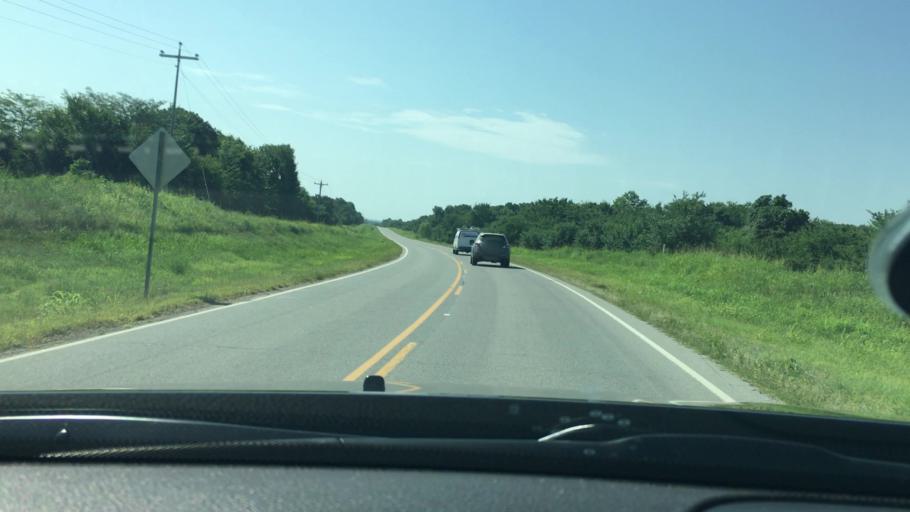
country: US
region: Oklahoma
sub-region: Coal County
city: Coalgate
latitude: 34.5922
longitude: -96.4234
